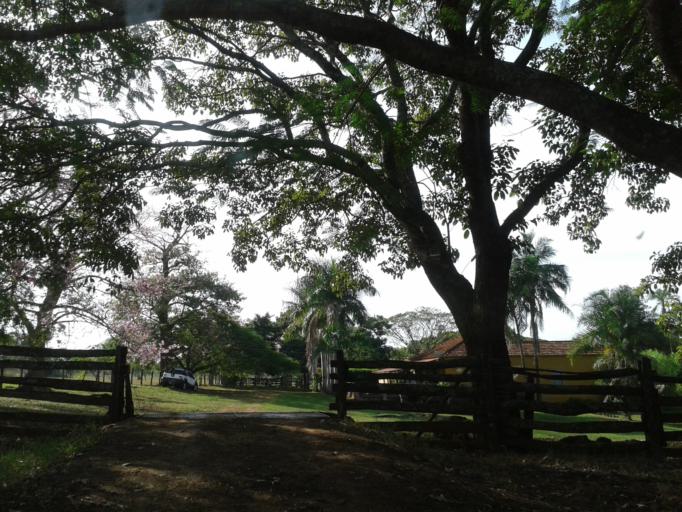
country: BR
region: Minas Gerais
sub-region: Campina Verde
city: Campina Verde
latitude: -19.5246
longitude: -49.6106
